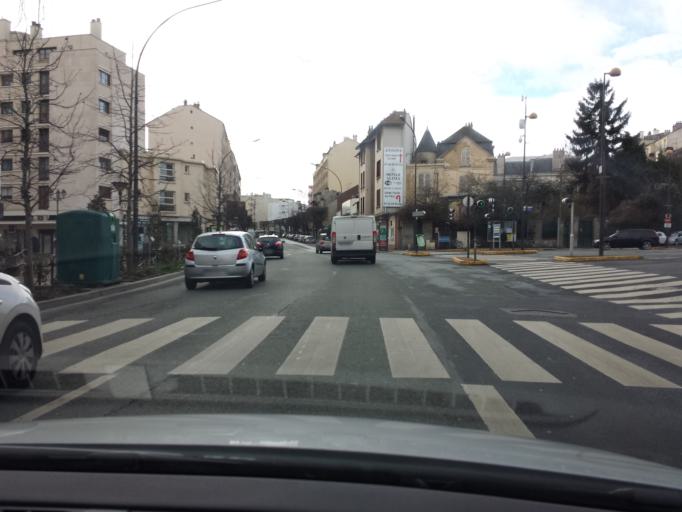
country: FR
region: Ile-de-France
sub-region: Departement des Hauts-de-Seine
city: Bourg-la-Reine
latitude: 48.7803
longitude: 2.3137
